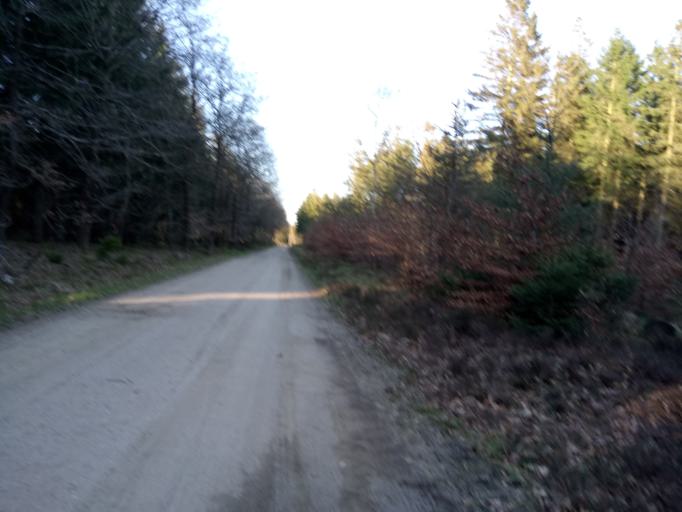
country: DK
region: Central Jutland
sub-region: Ringkobing-Skjern Kommune
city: Skjern
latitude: 56.0024
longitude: 8.4500
